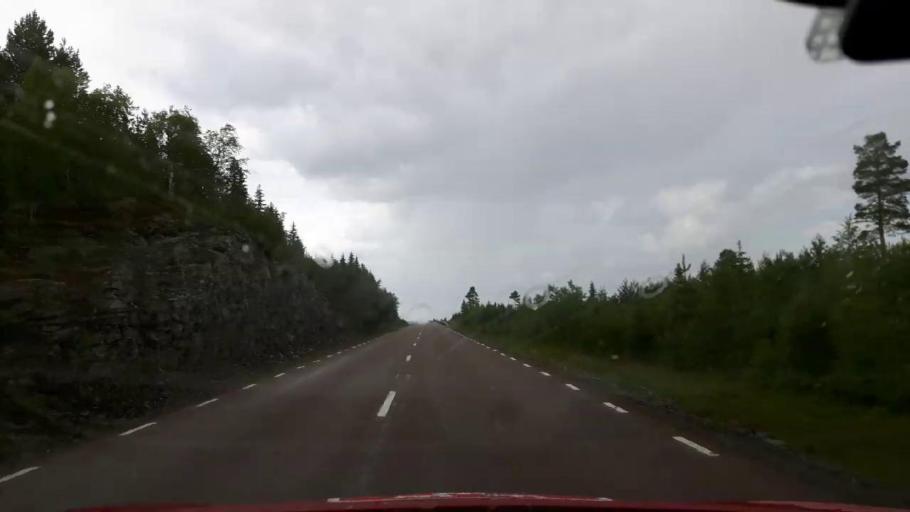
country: SE
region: Jaemtland
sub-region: Krokoms Kommun
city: Krokom
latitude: 63.8855
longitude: 14.2817
